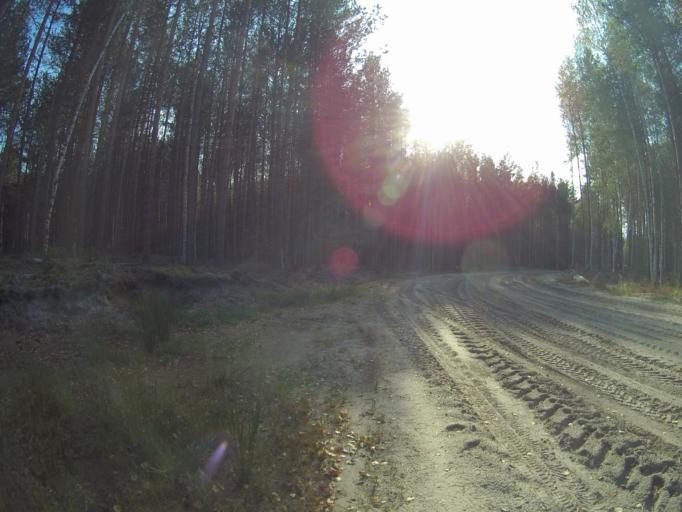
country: RU
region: Vladimir
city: Urshel'skiy
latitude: 55.8065
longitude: 40.1452
